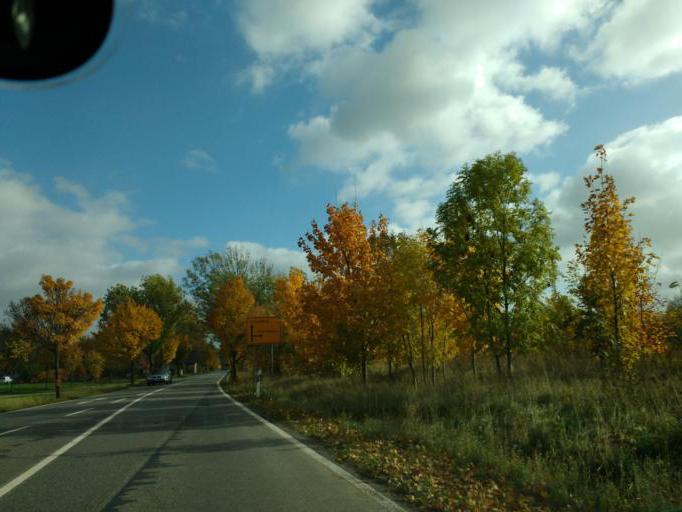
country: DE
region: Brandenburg
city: Altlandsberg
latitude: 52.5603
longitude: 13.7678
